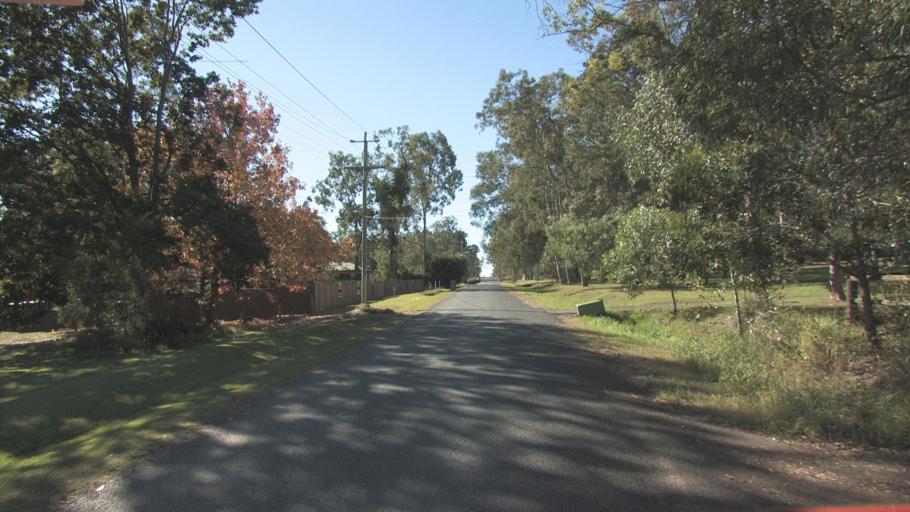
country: AU
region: Queensland
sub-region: Logan
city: Park Ridge South
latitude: -27.7316
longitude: 153.0113
